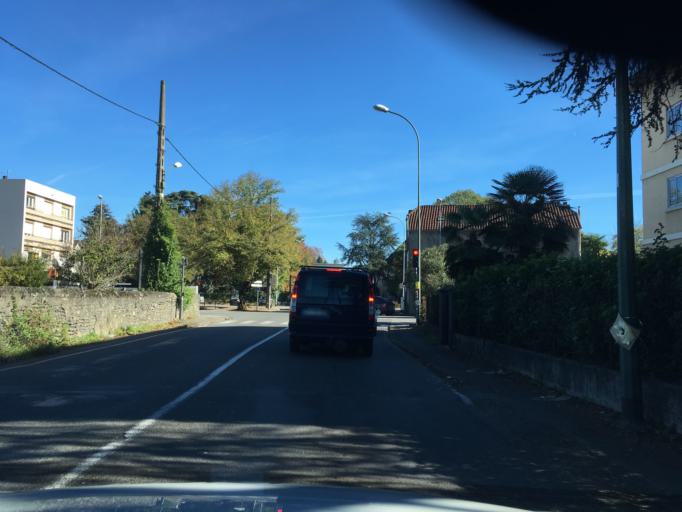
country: FR
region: Aquitaine
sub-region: Departement des Pyrenees-Atlantiques
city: Pau
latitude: 43.3095
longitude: -0.3447
